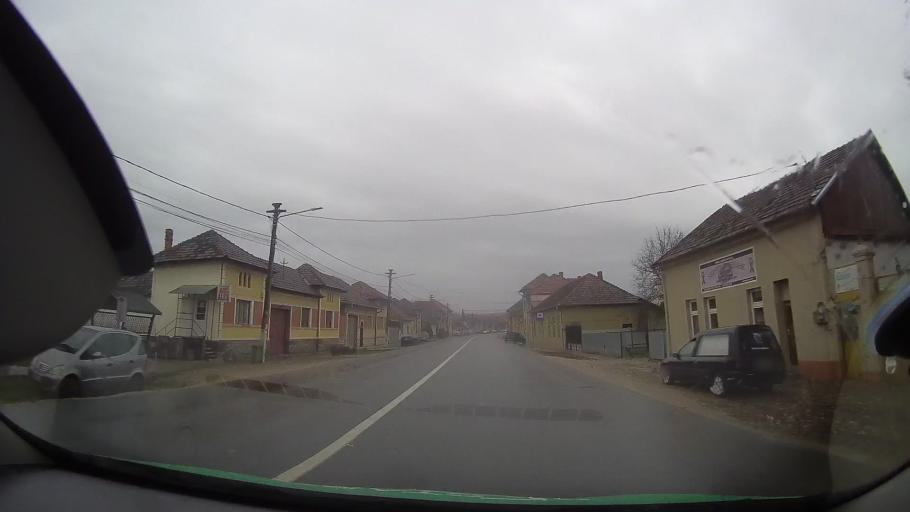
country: RO
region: Bihor
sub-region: Comuna Pocola
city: Pocola
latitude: 46.6952
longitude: 22.2924
